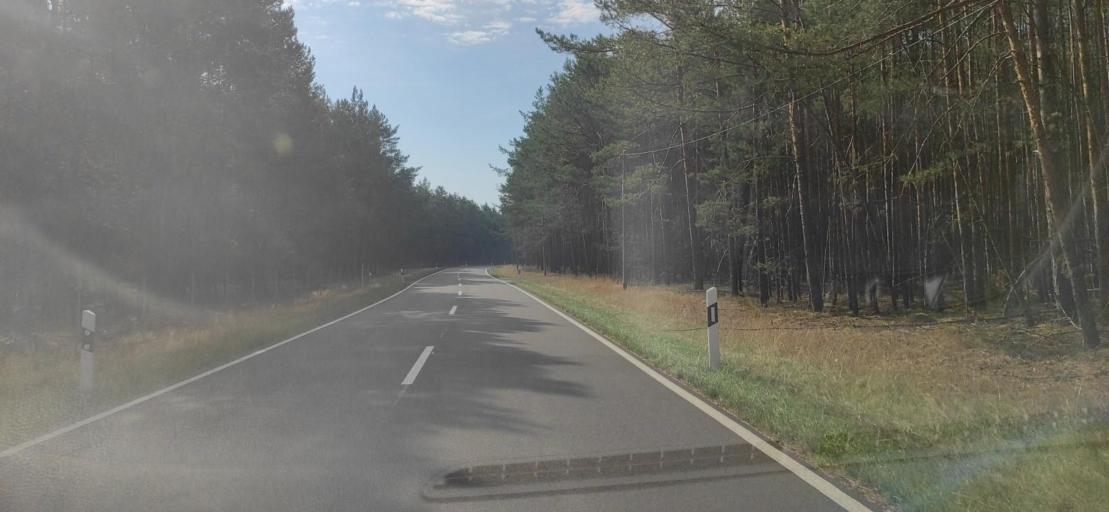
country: PL
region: Lubusz
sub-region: Powiat zarski
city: Trzebiel
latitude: 51.6272
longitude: 14.7500
